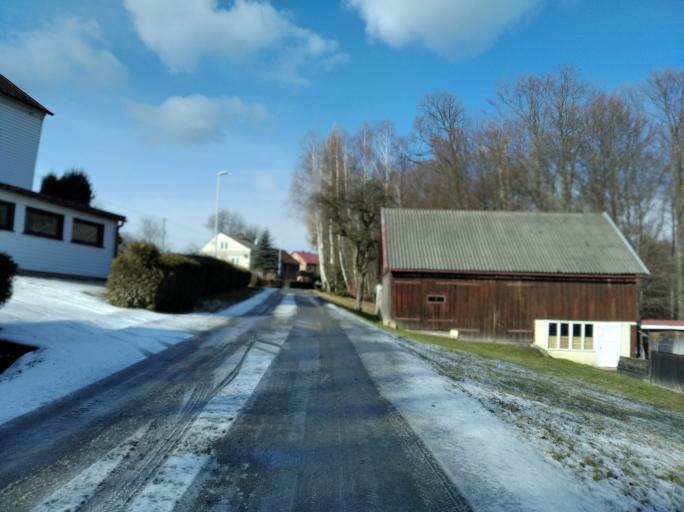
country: PL
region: Subcarpathian Voivodeship
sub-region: Powiat strzyzowski
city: Strzyzow
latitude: 49.8986
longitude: 21.7676
